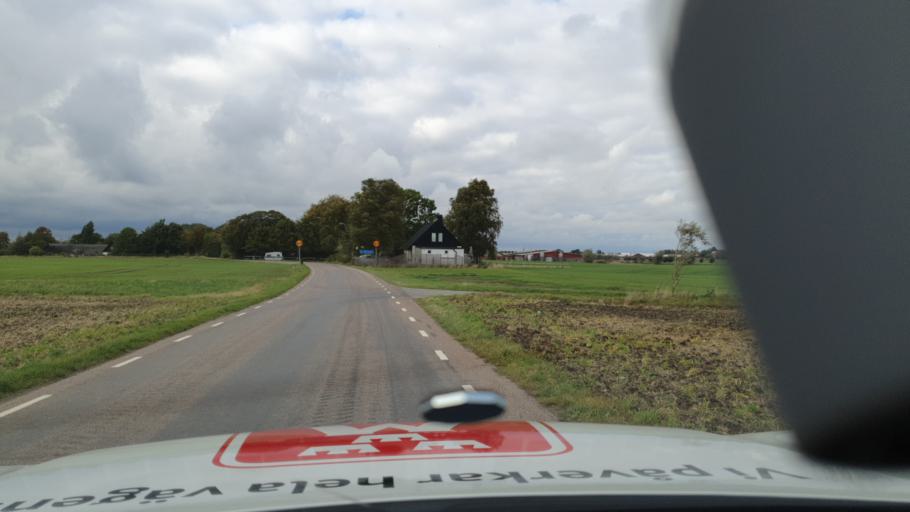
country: SE
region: Skane
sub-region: Trelleborgs Kommun
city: Skare
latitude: 55.4249
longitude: 13.0912
